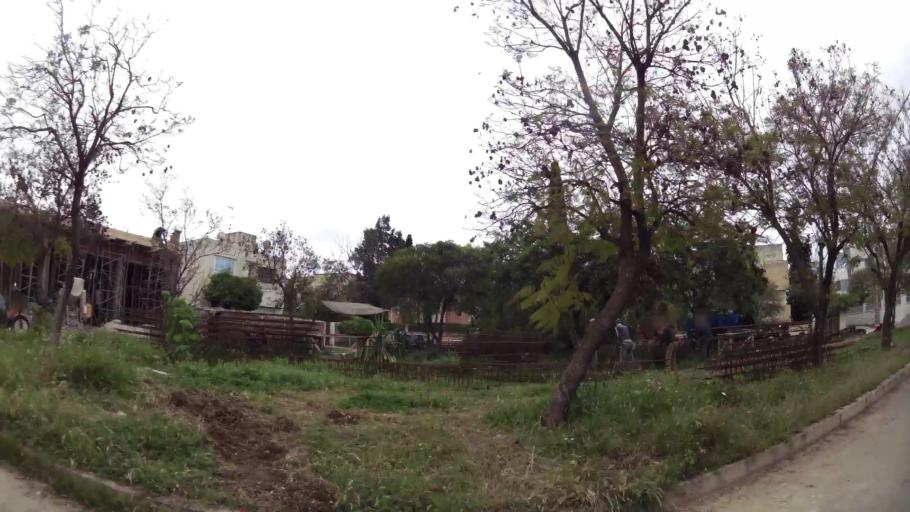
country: MA
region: Fes-Boulemane
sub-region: Fes
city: Fes
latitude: 34.0325
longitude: -5.0118
